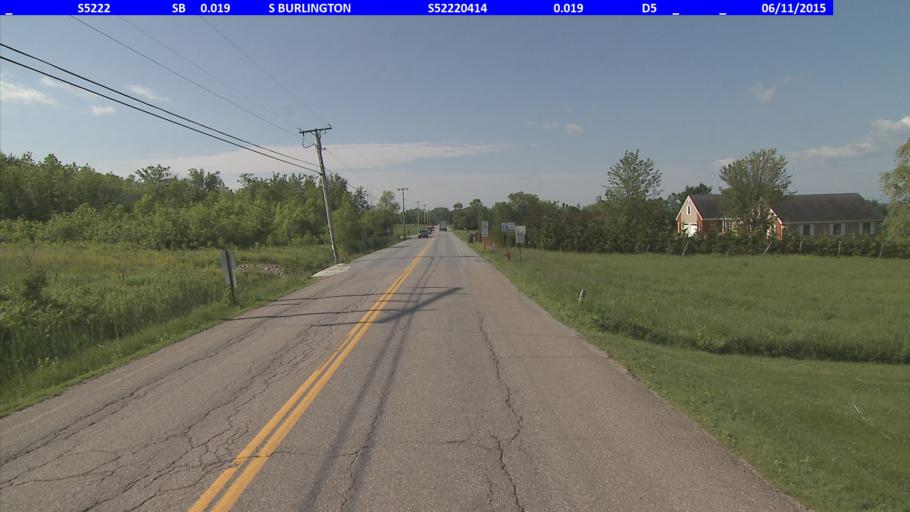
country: US
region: Vermont
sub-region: Chittenden County
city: South Burlington
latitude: 44.4169
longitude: -73.1967
